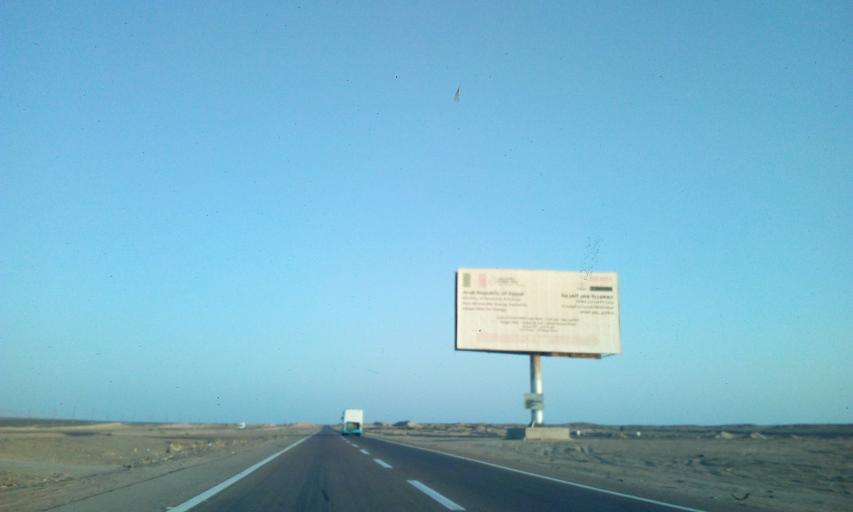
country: EG
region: South Sinai
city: Tor
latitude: 28.0495
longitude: 33.2802
